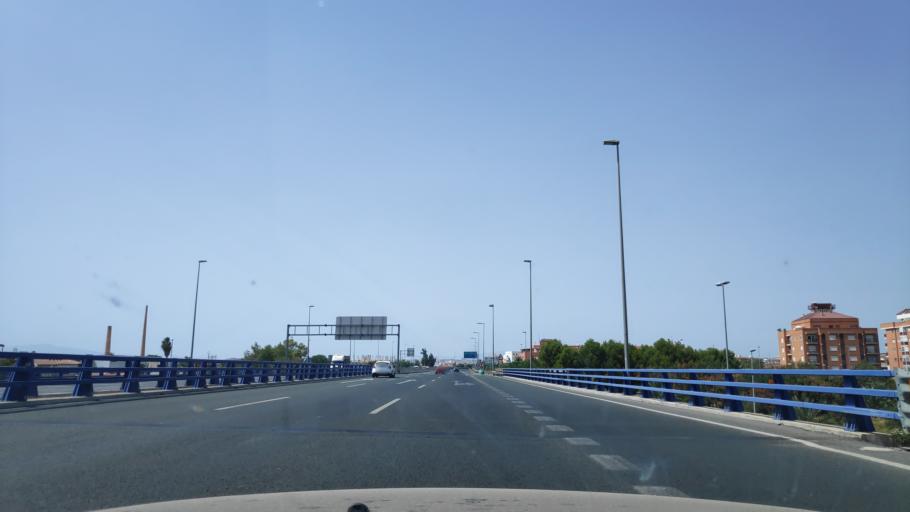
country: ES
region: Murcia
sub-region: Murcia
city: Murcia
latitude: 37.9660
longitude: -1.1366
